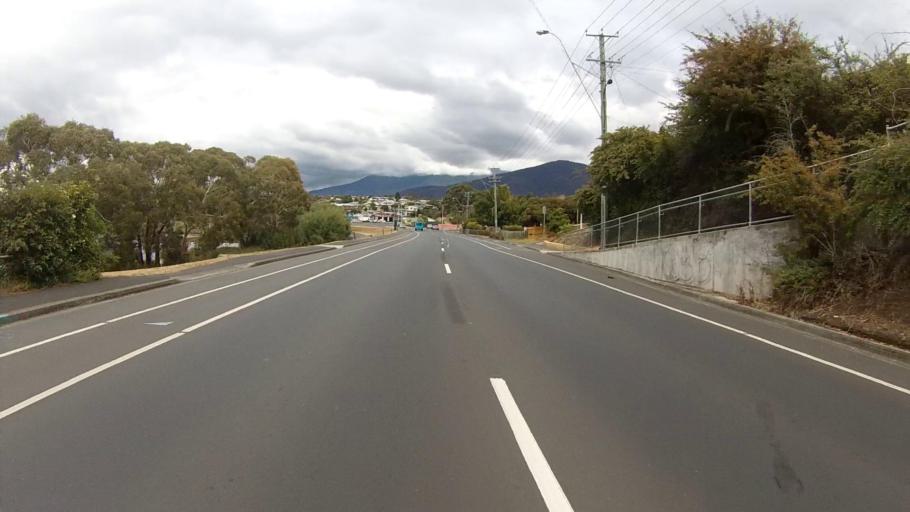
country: AU
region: Tasmania
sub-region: Glenorchy
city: Claremont
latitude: -42.7842
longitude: 147.2522
